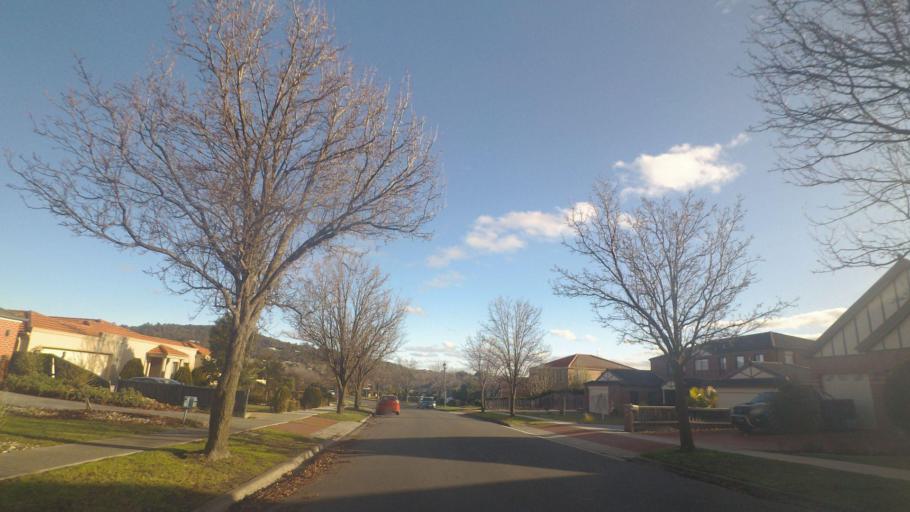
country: AU
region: Victoria
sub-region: Yarra Ranges
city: Lysterfield
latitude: -37.9165
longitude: 145.2879
